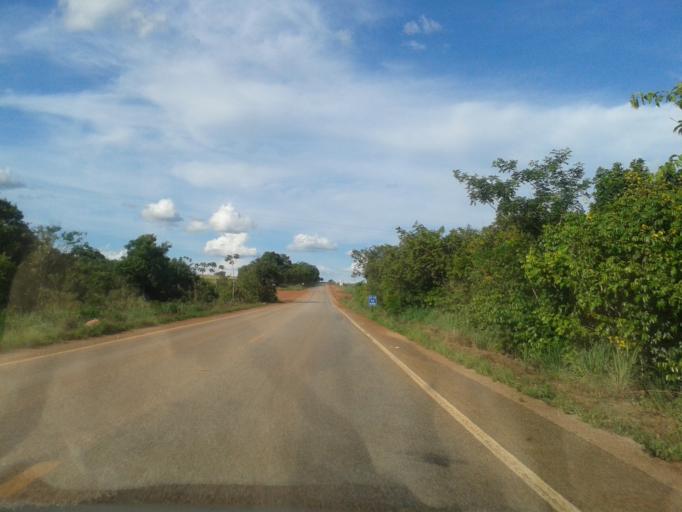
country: BR
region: Goias
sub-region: Mozarlandia
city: Mozarlandia
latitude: -14.4013
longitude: -50.4429
